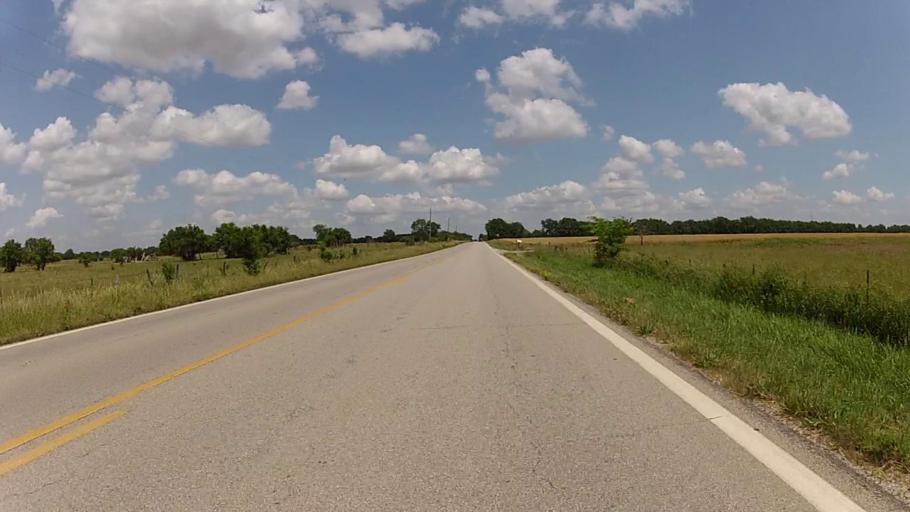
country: US
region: Kansas
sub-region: Labette County
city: Altamont
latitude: 37.1928
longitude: -95.3344
